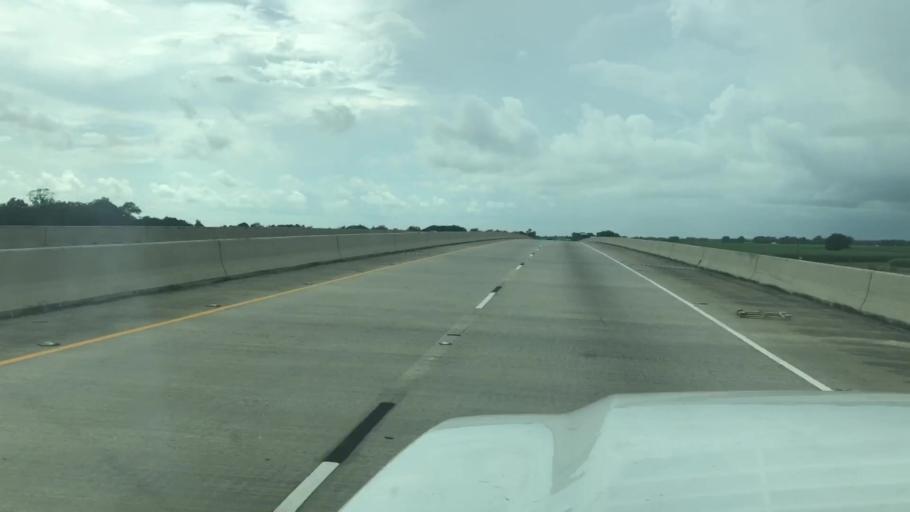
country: US
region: Louisiana
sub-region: Iberia Parish
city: Jeanerette
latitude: 29.9192
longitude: -91.7276
